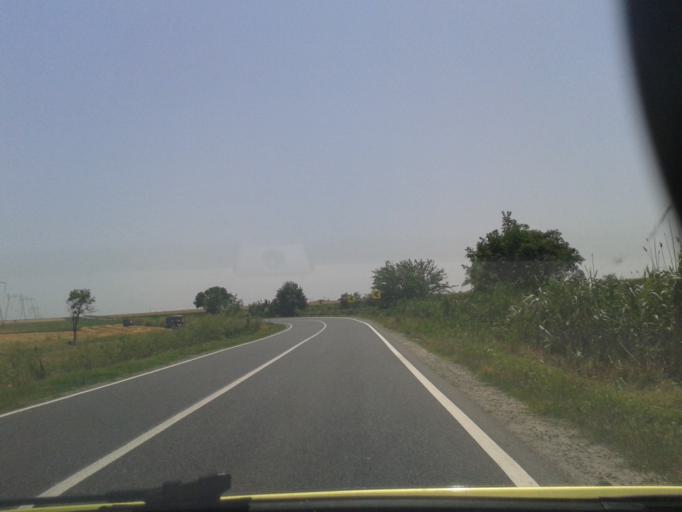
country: RO
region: Constanta
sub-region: Comuna Mihail Kogalniceanu
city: Mihail Kogalniceanu
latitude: 44.3573
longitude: 28.5189
